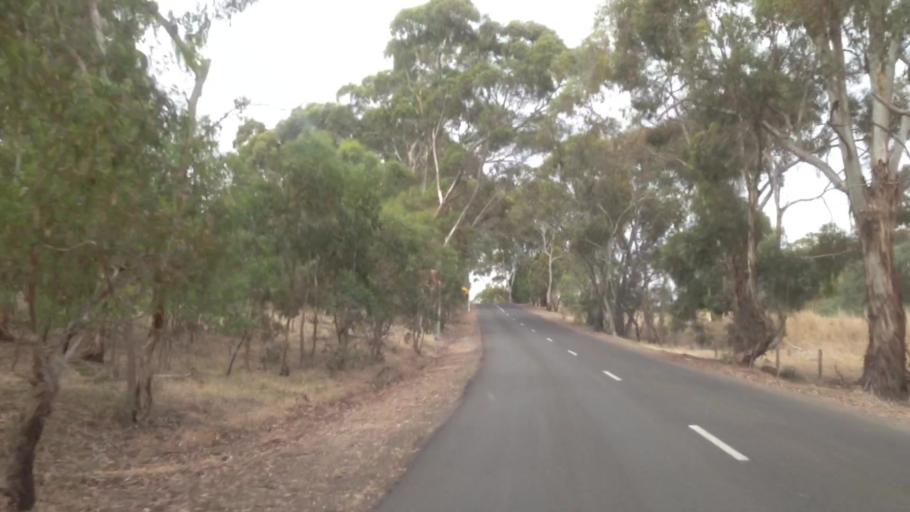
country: AU
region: South Australia
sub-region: Barossa
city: Williamstown
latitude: -34.6424
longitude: 138.8539
